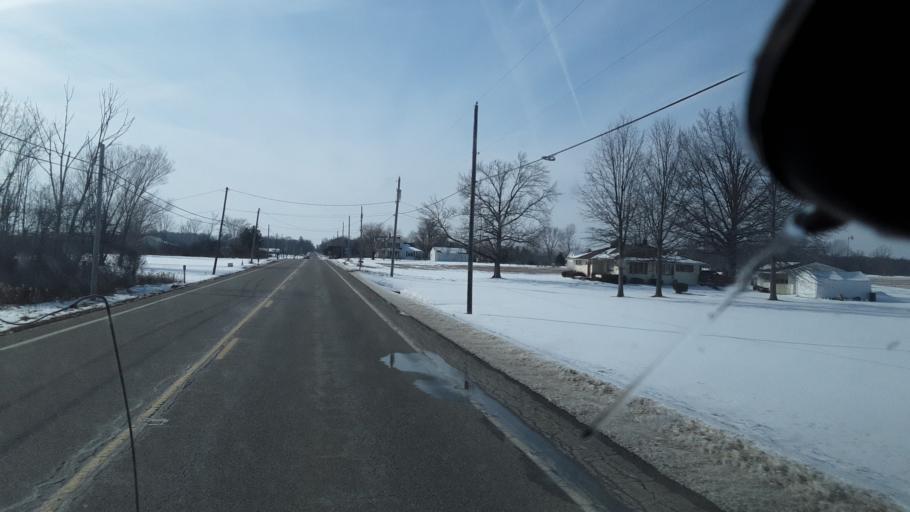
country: US
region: Ohio
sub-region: Mahoning County
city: Sebring
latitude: 41.0247
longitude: -81.0301
